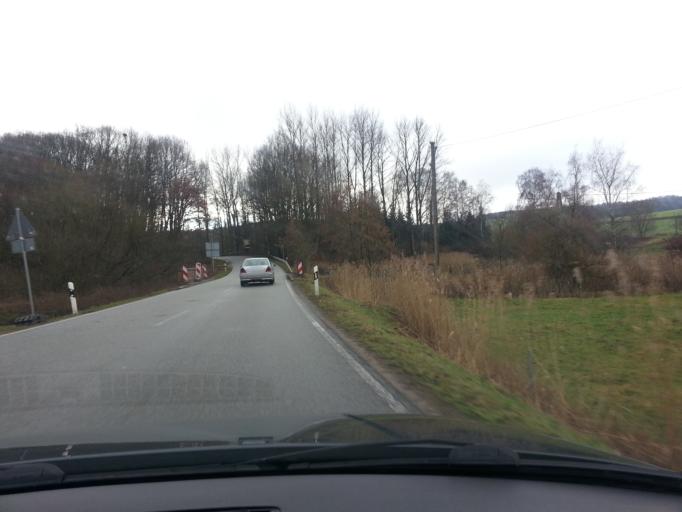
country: DE
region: Rheinland-Pfalz
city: Reichenbach-Steegen
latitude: 49.4965
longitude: 7.5516
